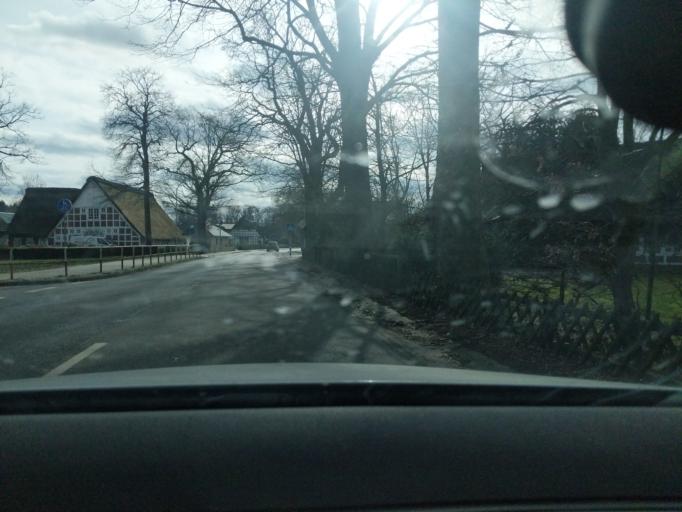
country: DE
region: Lower Saxony
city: Himmelpforten
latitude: 53.6185
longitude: 9.3159
